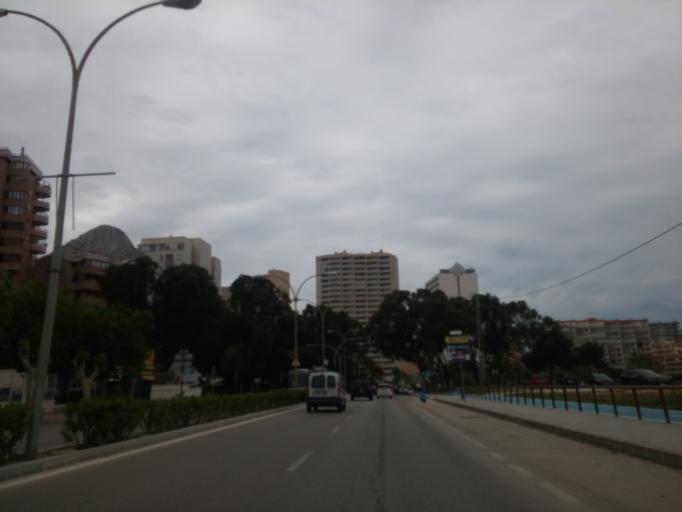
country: ES
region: Valencia
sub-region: Provincia de Alicante
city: Calp
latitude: 38.6452
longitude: 0.0711
